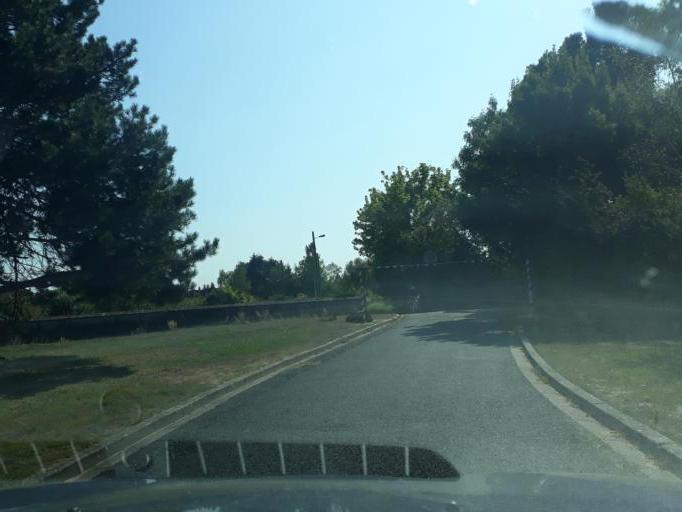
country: FR
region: Centre
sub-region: Departement de l'Indre
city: Chabris
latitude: 47.2588
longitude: 1.6542
